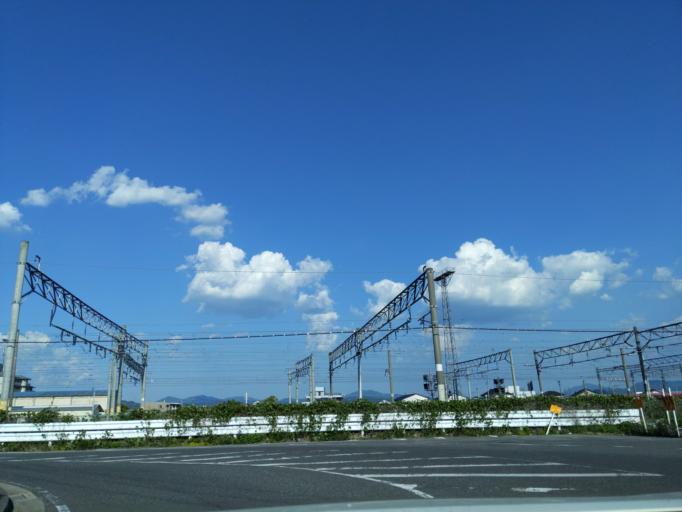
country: JP
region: Fukushima
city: Koriyama
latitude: 37.3730
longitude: 140.3758
